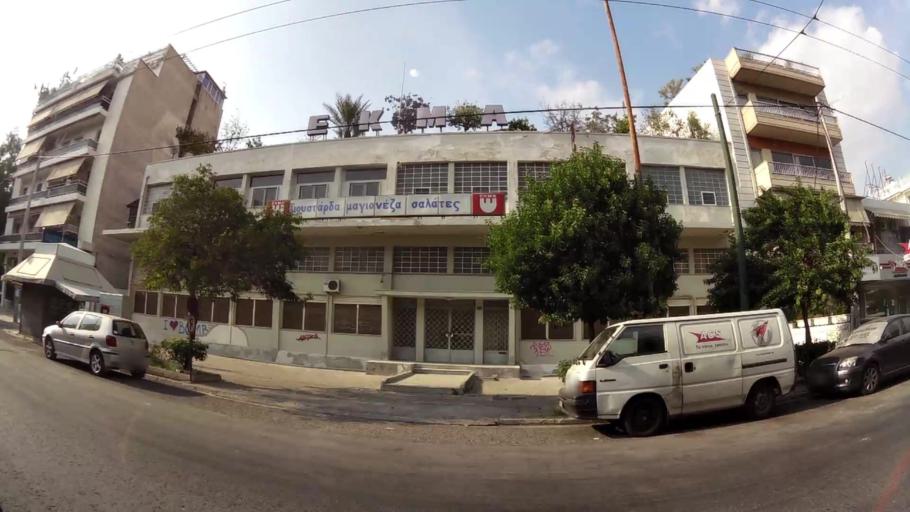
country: GR
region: Attica
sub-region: Nomarchia Athinas
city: Kallithea
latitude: 37.9484
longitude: 23.6896
